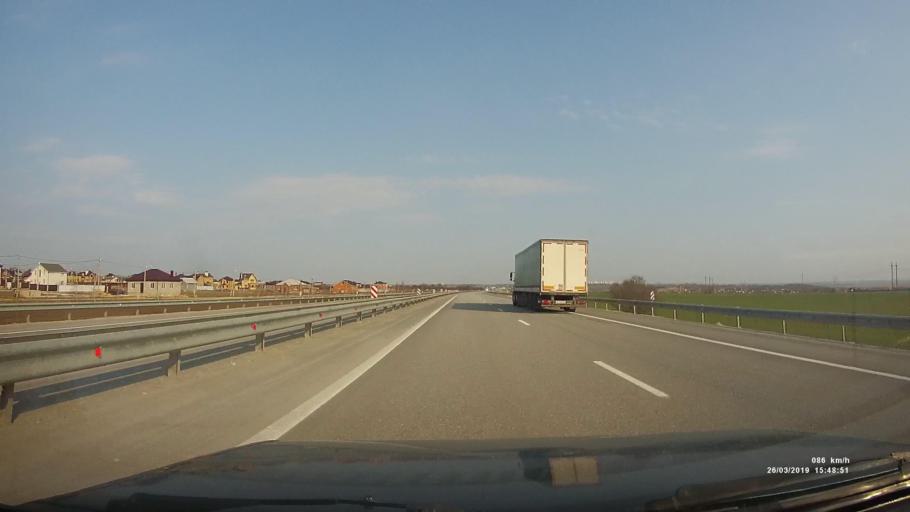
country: RU
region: Rostov
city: Chaltyr
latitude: 47.2779
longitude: 39.4591
